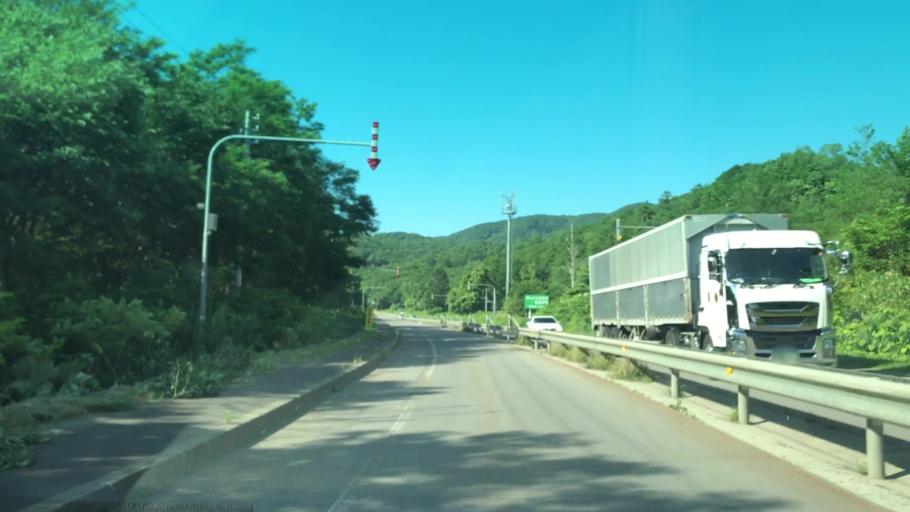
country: JP
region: Hokkaido
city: Iwanai
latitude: 42.9960
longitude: 140.6670
